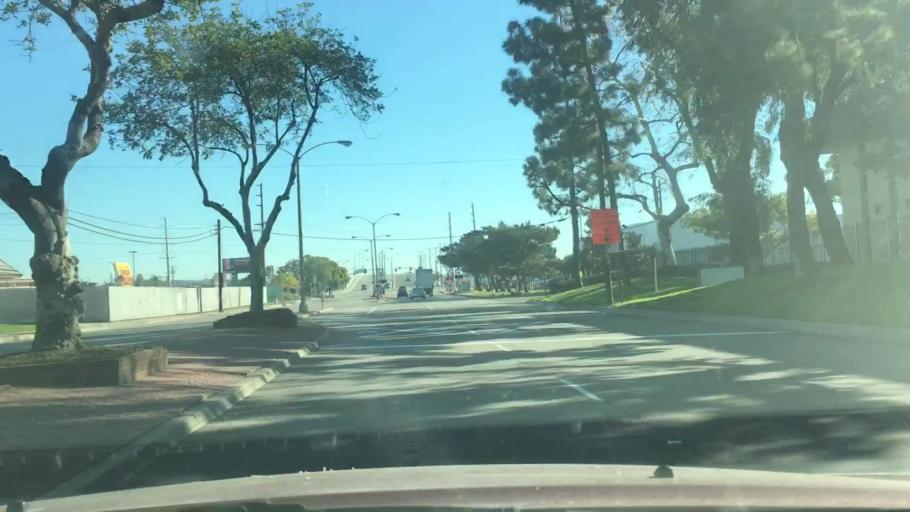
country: US
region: California
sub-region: Los Angeles County
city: Cerritos
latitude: 33.8879
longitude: -118.0410
